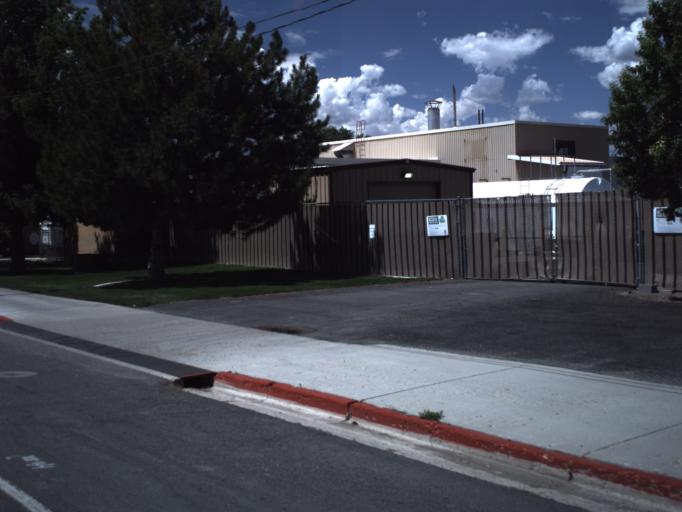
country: US
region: Utah
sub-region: Sanpete County
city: Ephraim
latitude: 39.3616
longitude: -111.5802
